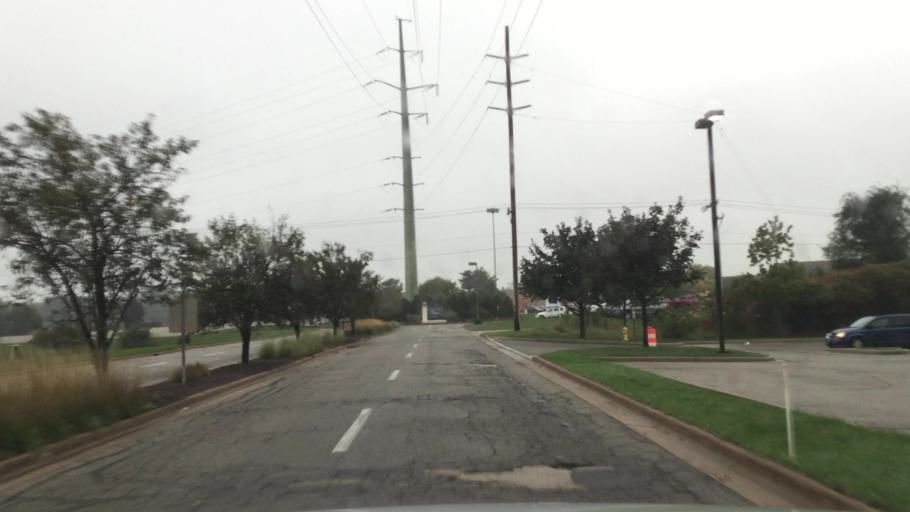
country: US
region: Michigan
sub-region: Kalamazoo County
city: Portage
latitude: 42.2195
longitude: -85.5900
